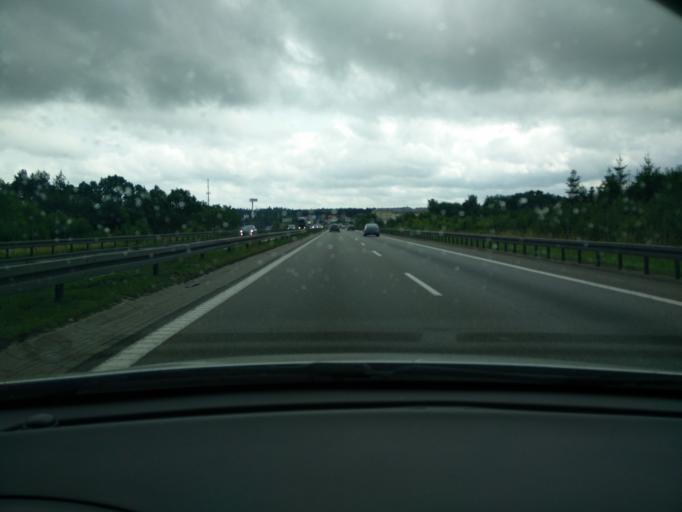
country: PL
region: Pomeranian Voivodeship
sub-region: Gdynia
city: Wielki Kack
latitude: 54.4781
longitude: 18.4724
